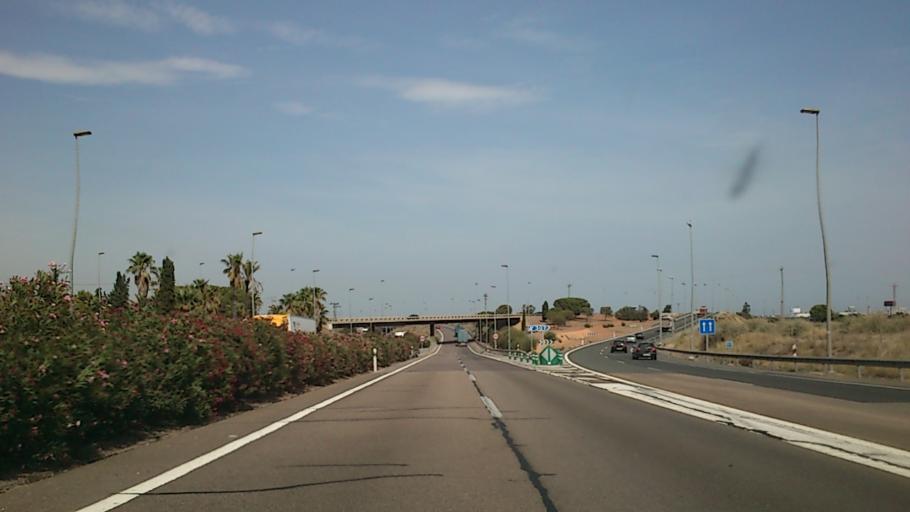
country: ES
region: Valencia
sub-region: Provincia de Valencia
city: Pucol
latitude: 39.6308
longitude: -0.3083
